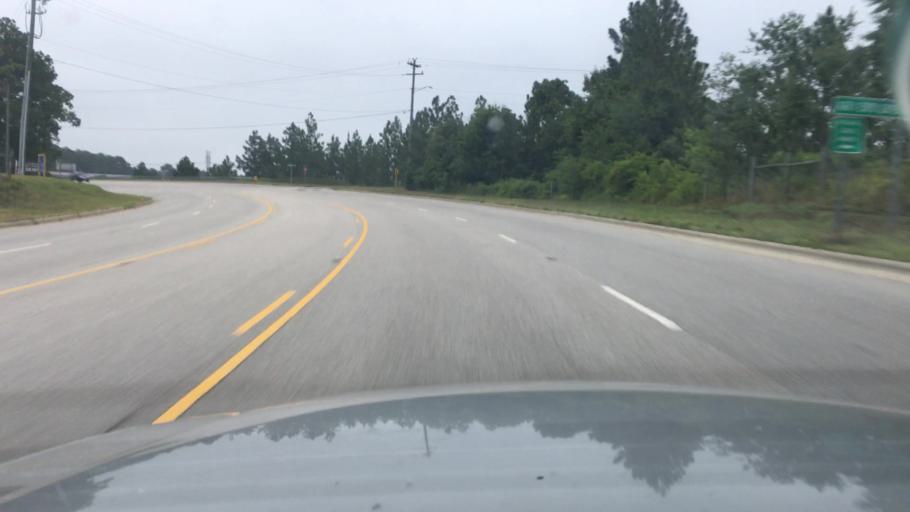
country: US
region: North Carolina
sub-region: Cumberland County
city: Fayetteville
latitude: 35.0126
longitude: -78.8887
